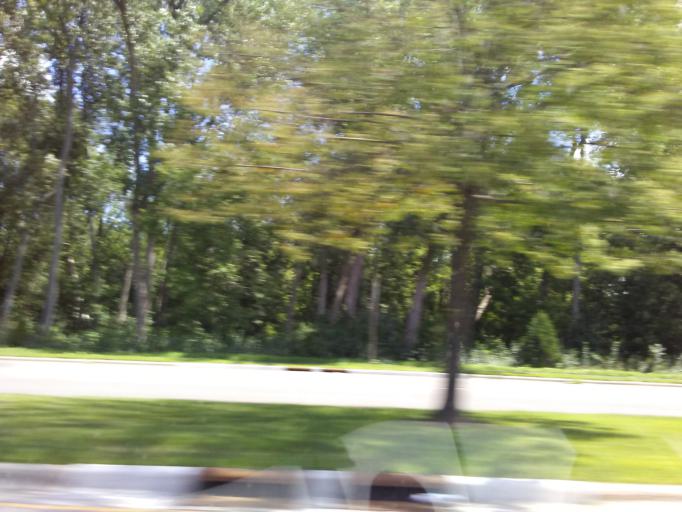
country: US
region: Wisconsin
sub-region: Dane County
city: Middleton
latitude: 43.0975
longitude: -89.4862
